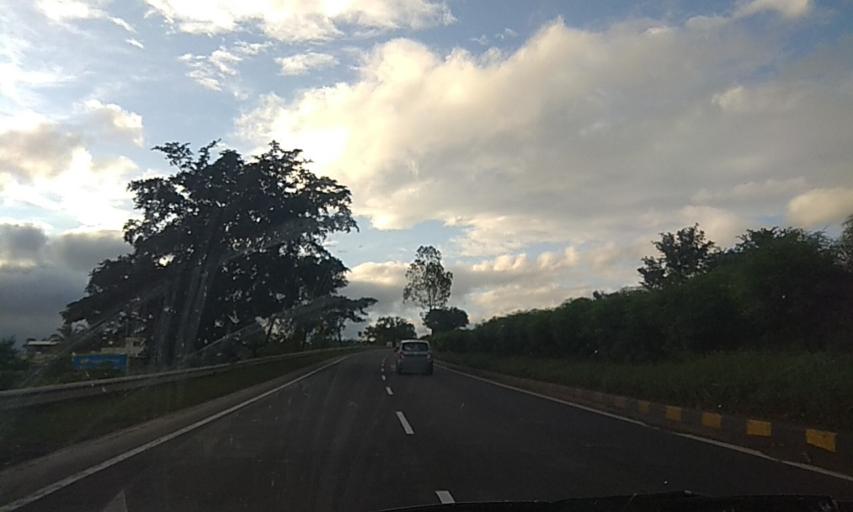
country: IN
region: Maharashtra
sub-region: Satara Division
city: Satara
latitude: 17.5971
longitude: 74.0381
